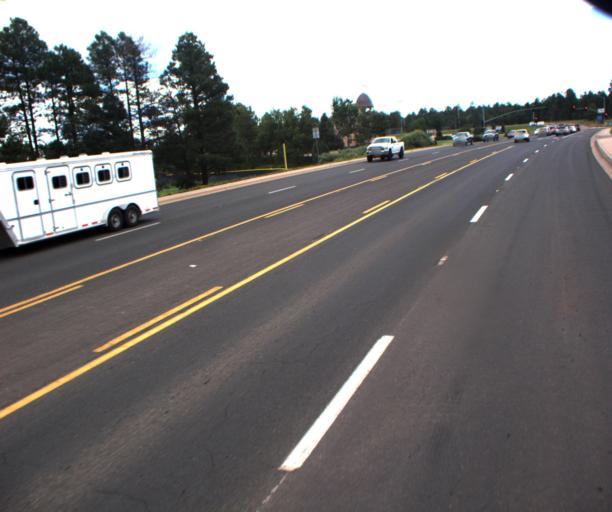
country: US
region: Arizona
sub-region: Navajo County
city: Show Low
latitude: 34.2423
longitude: -110.0603
